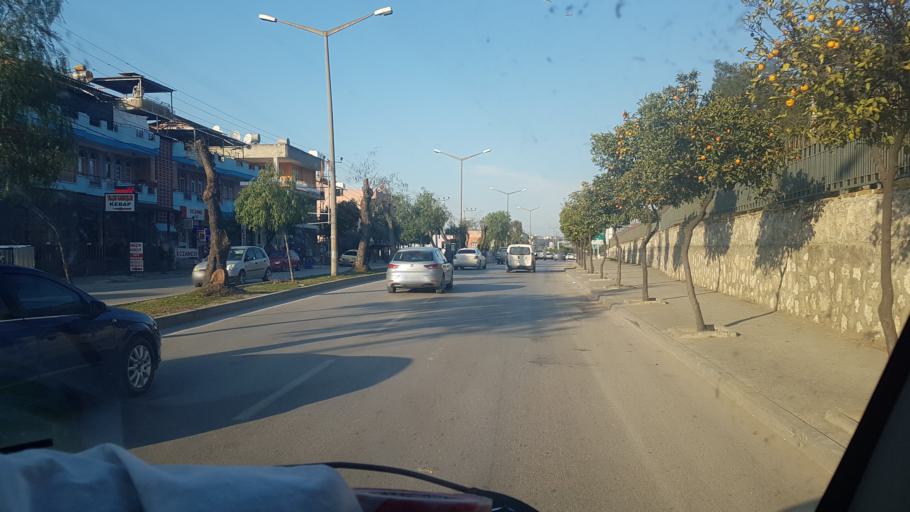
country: TR
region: Adana
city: Adana
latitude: 37.0178
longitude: 35.3407
